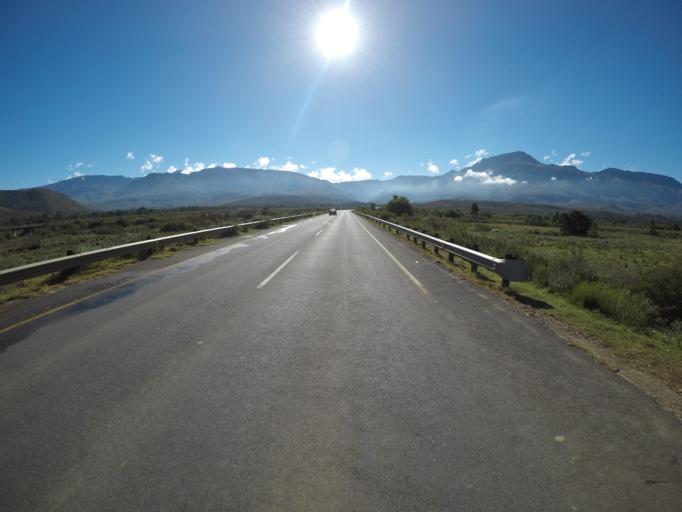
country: ZA
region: Western Cape
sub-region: Overberg District Municipality
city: Caledon
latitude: -34.0644
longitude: 19.5584
